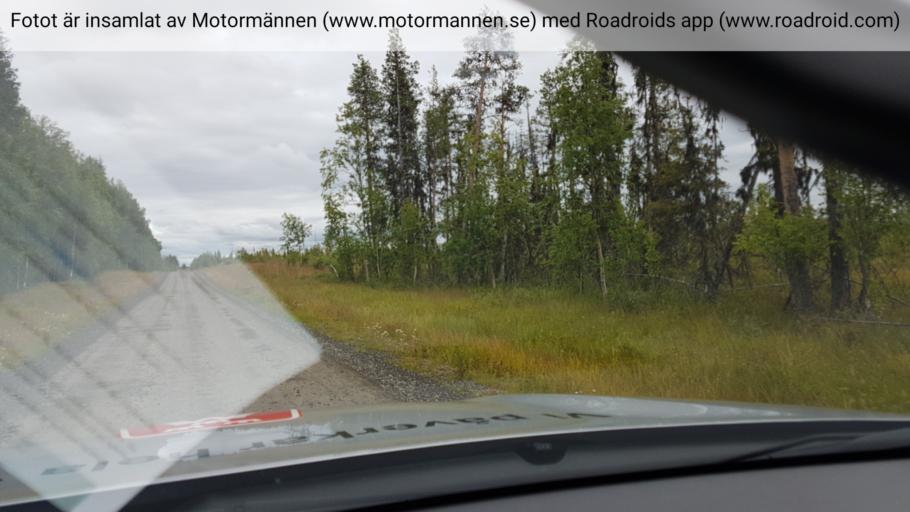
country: SE
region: Norrbotten
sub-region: Pajala Kommun
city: Pajala
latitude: 67.0836
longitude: 22.7717
